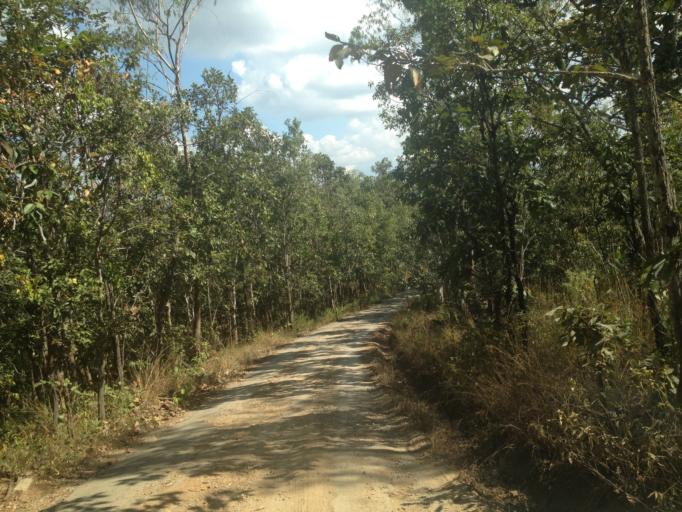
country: TH
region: Mae Hong Son
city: Ban Huai I Huak
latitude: 18.1079
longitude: 98.1858
